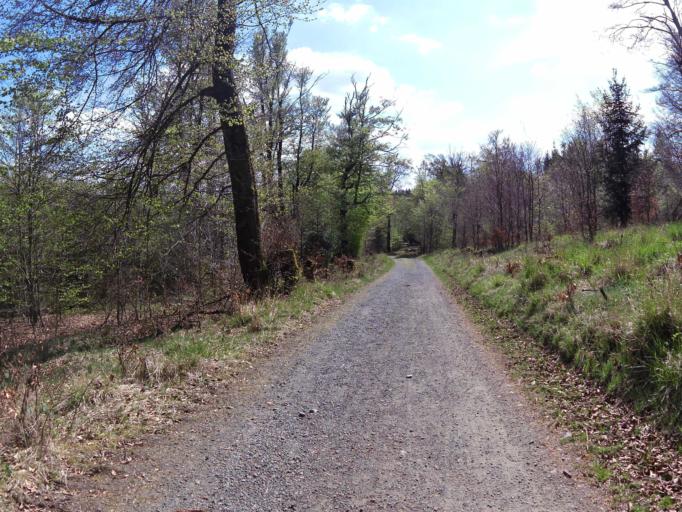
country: DE
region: Thuringia
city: Friedrichroda
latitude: 50.8154
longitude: 10.5421
